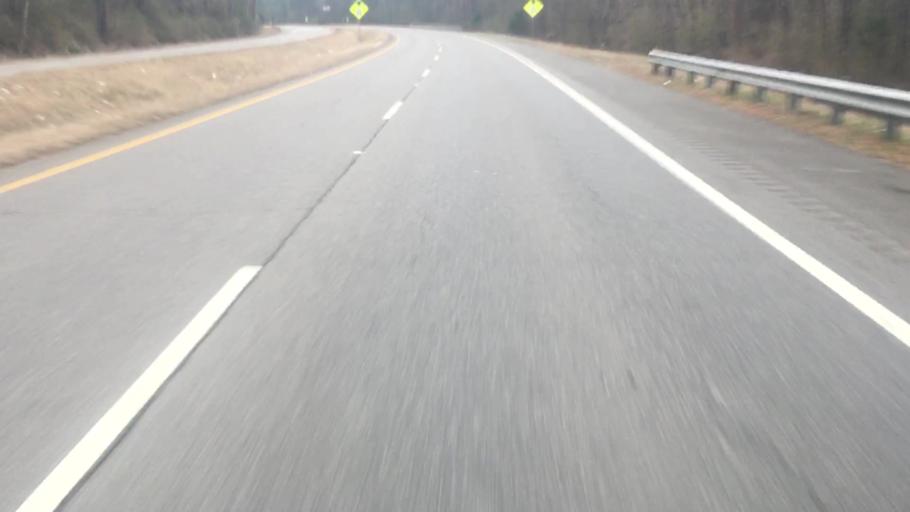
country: US
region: Alabama
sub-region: Walker County
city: Cordova
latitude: 33.8221
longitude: -87.1883
